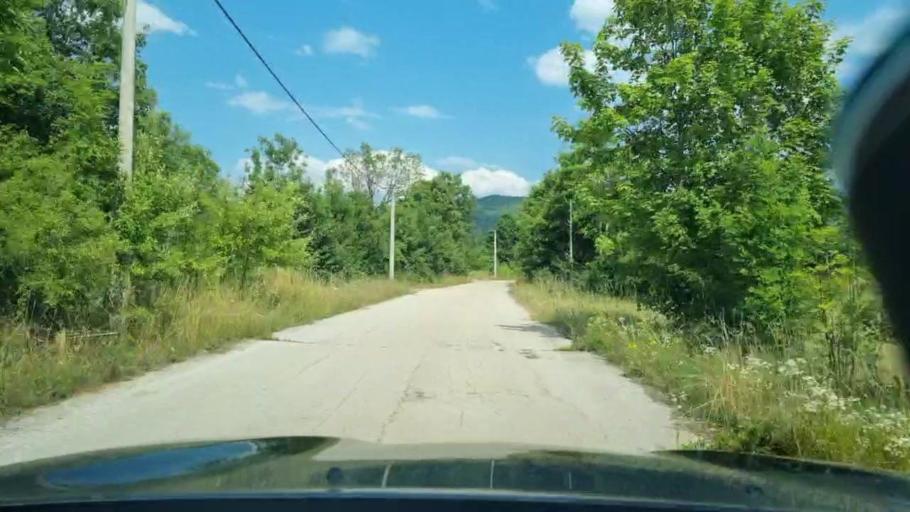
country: BA
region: Federation of Bosnia and Herzegovina
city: Bosansko Grahovo
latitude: 44.2946
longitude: 16.2902
